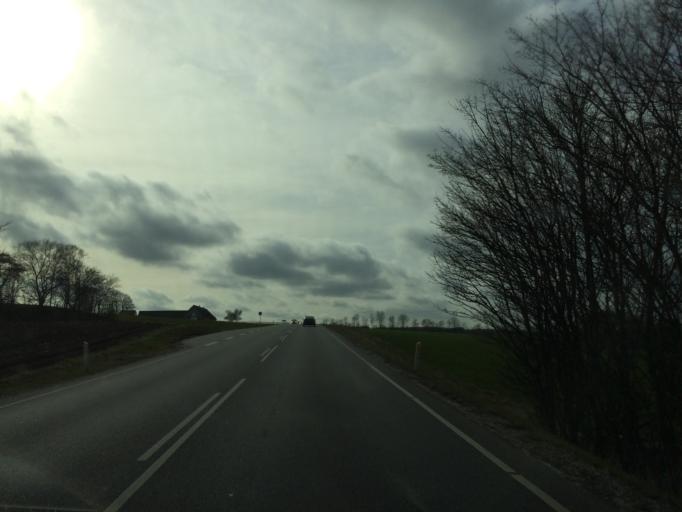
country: DK
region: Central Jutland
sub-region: Norddjurs Kommune
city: Allingabro
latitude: 56.4466
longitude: 10.2717
